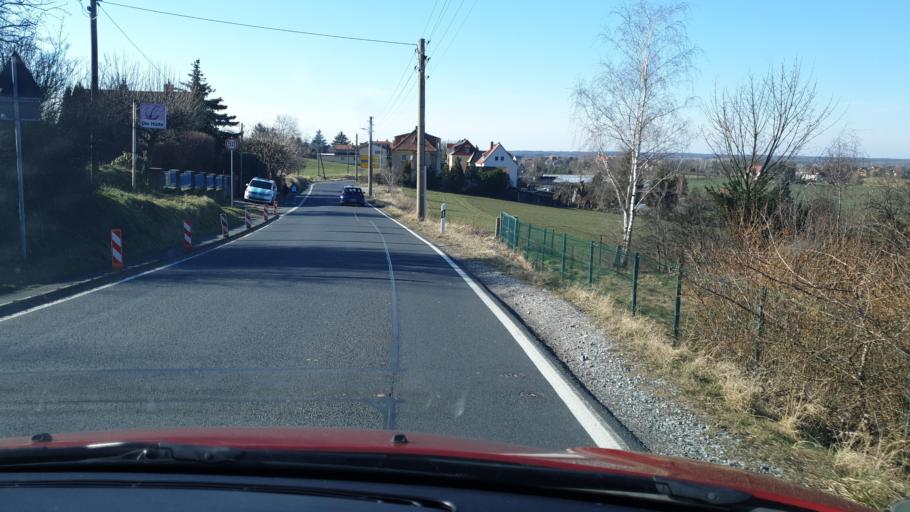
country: DE
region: Saxony
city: Radebeul
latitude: 51.1225
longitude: 13.6935
